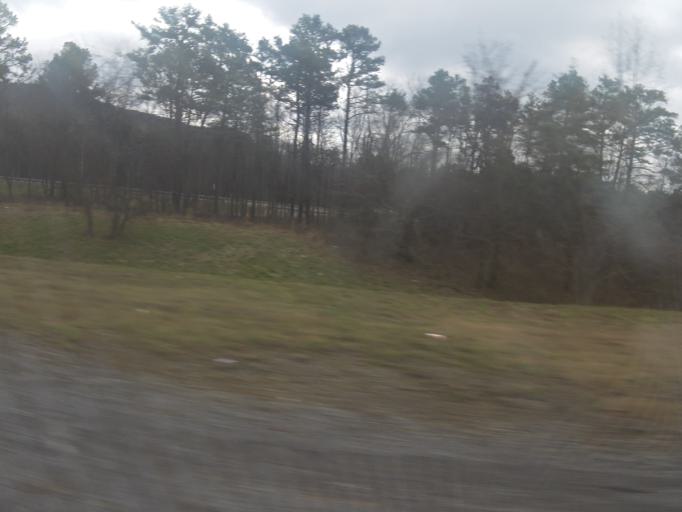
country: US
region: Georgia
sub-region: Walker County
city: Lookout Mountain
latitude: 34.9739
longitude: -85.4545
